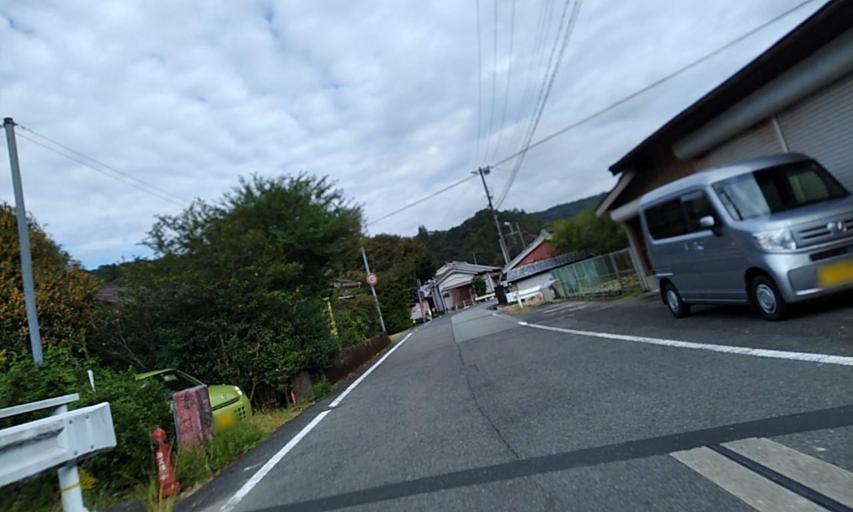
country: JP
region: Wakayama
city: Shingu
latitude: 33.5388
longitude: 135.8216
